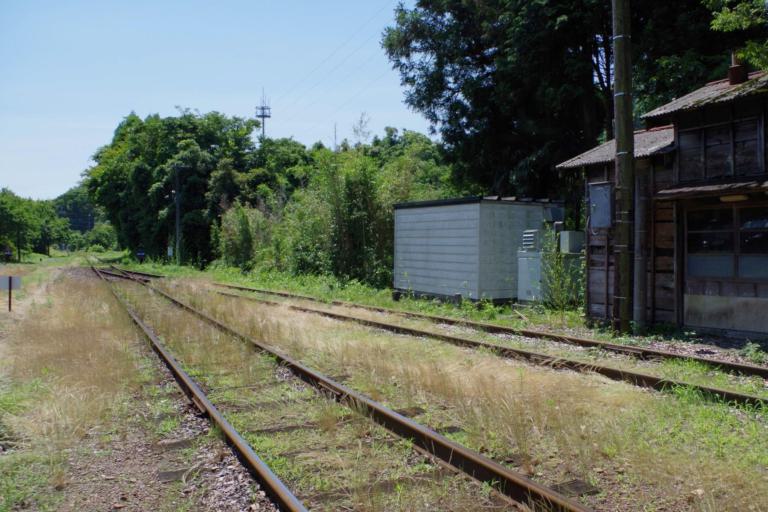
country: JP
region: Chiba
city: Katsuura
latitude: 35.2499
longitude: 140.1999
